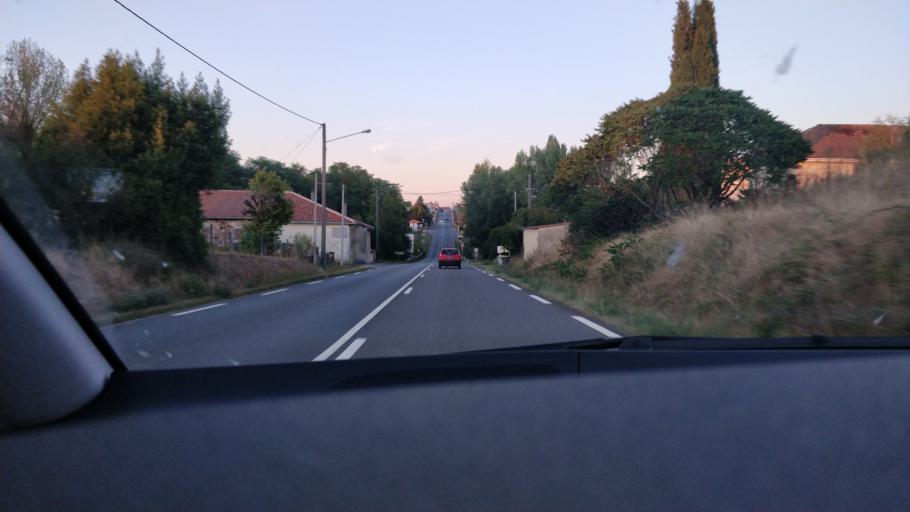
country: FR
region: Poitou-Charentes
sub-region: Departement de la Charente
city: Loubert
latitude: 45.8812
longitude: 0.5696
